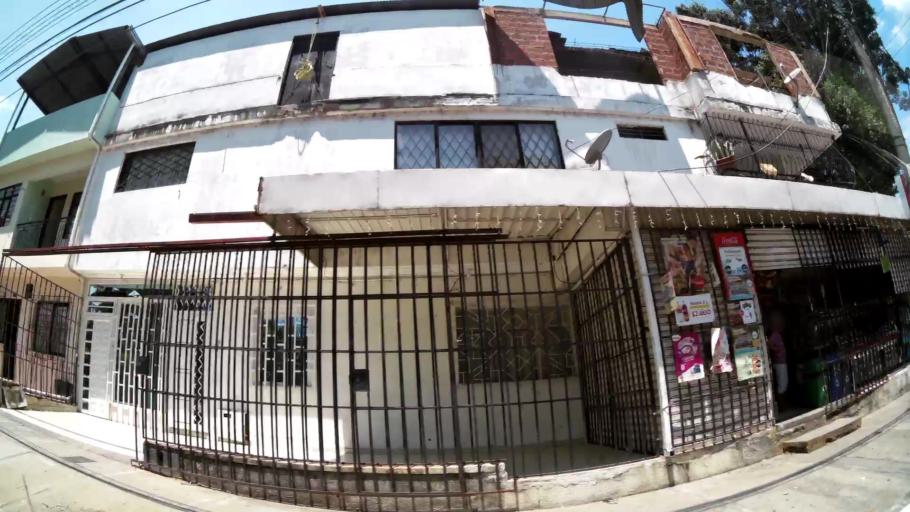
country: CO
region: Valle del Cauca
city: Cali
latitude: 3.4507
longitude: -76.4961
